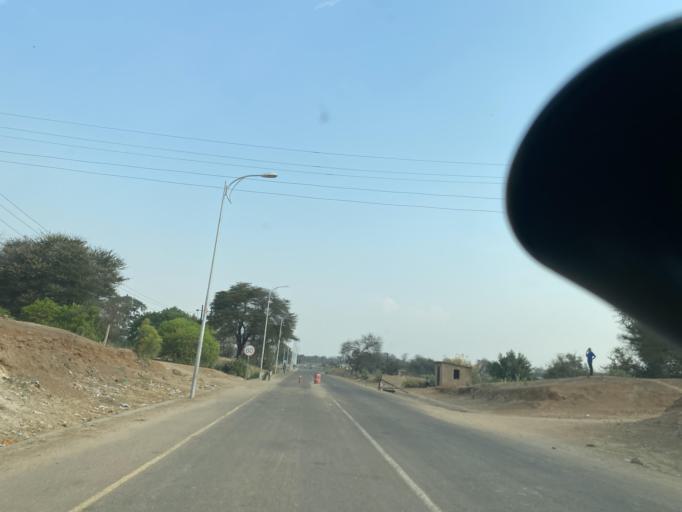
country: ZW
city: Chirundu
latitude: -15.9431
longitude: 28.8745
